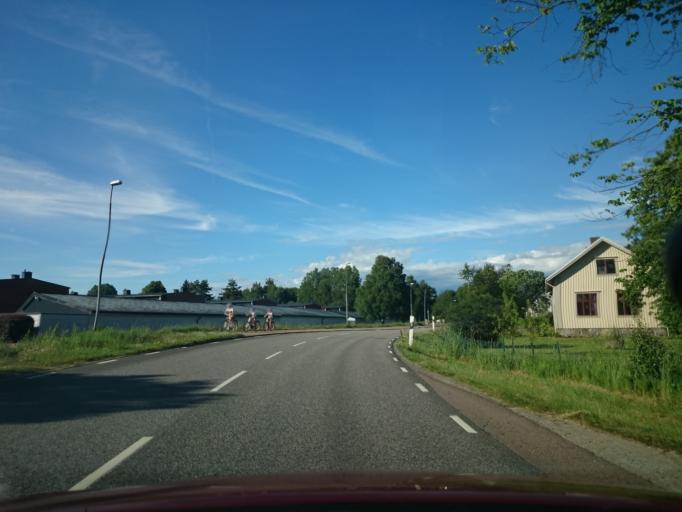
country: SE
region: Vaestra Goetaland
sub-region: Lerums Kommun
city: Stenkullen
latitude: 57.7883
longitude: 12.3088
